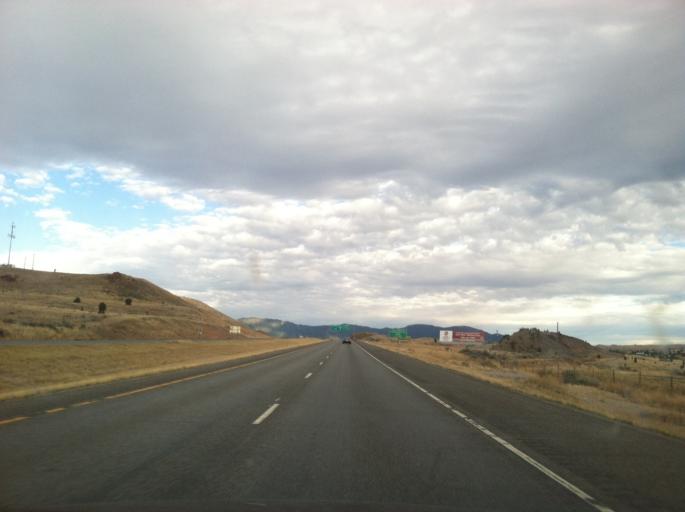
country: US
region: Montana
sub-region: Silver Bow County
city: Butte-Silver Bow (Balance)
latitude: 46.0075
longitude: -112.6612
